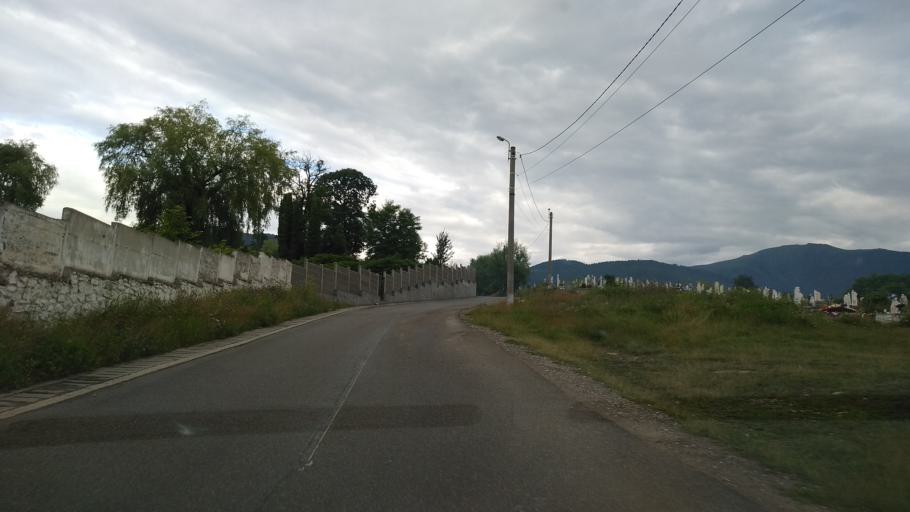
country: RO
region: Hunedoara
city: Vulcan
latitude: 45.3689
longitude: 23.2826
